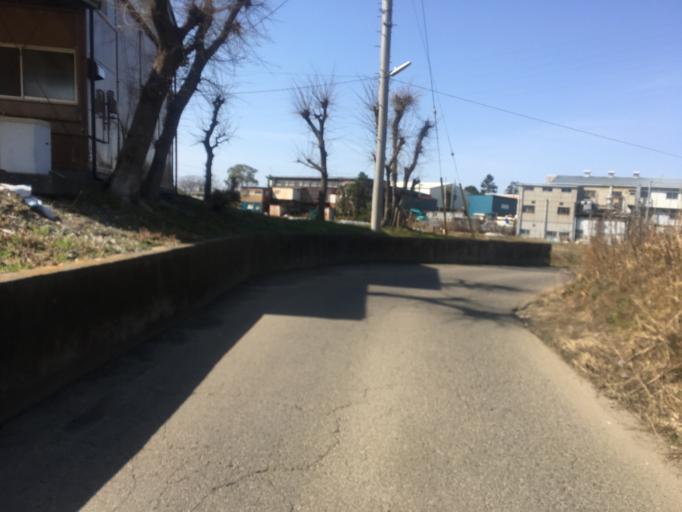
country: JP
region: Saitama
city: Shiki
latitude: 35.8296
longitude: 139.6055
